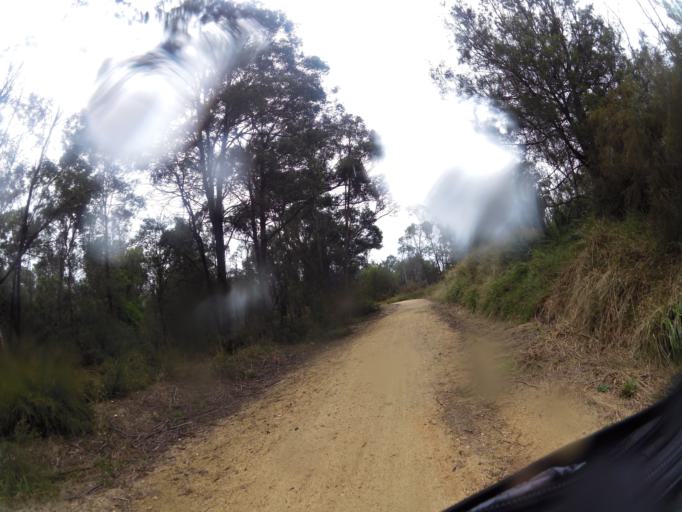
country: AU
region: Victoria
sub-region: East Gippsland
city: Bairnsdale
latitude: -37.7423
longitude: 147.8098
